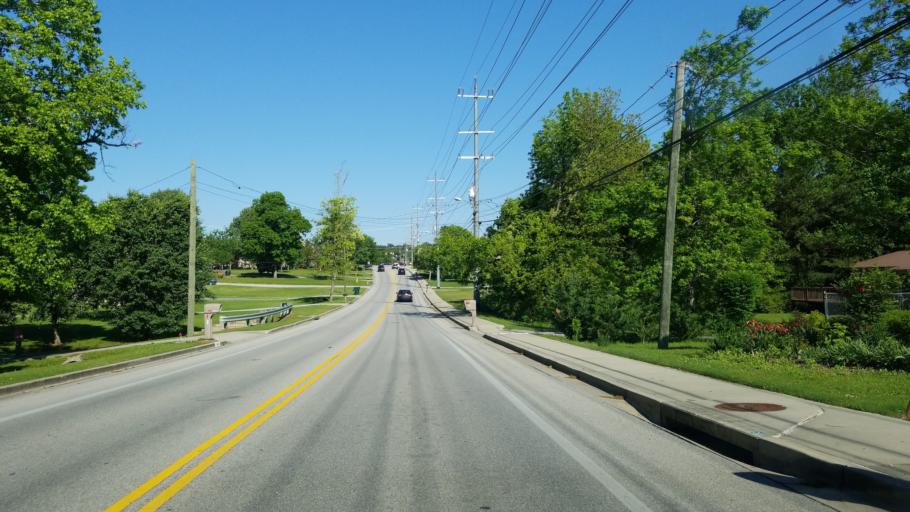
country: US
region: Tennessee
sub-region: Hamilton County
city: East Brainerd
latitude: 35.0255
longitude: -85.1535
